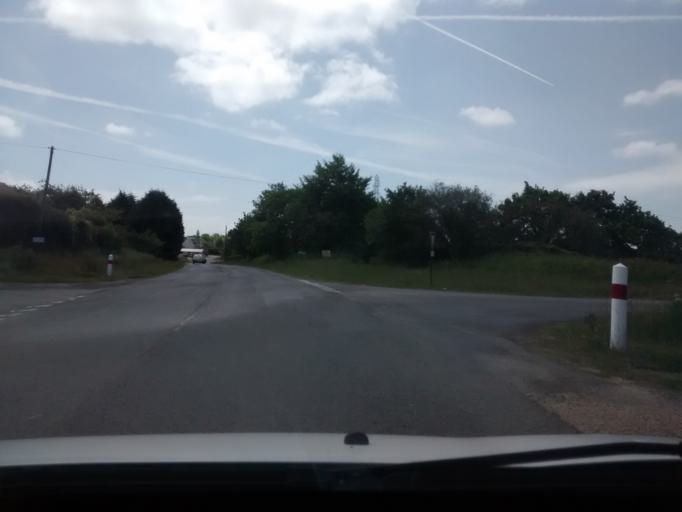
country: FR
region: Brittany
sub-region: Departement des Cotes-d'Armor
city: Saint-Quay-Perros
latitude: 48.7693
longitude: -3.4267
